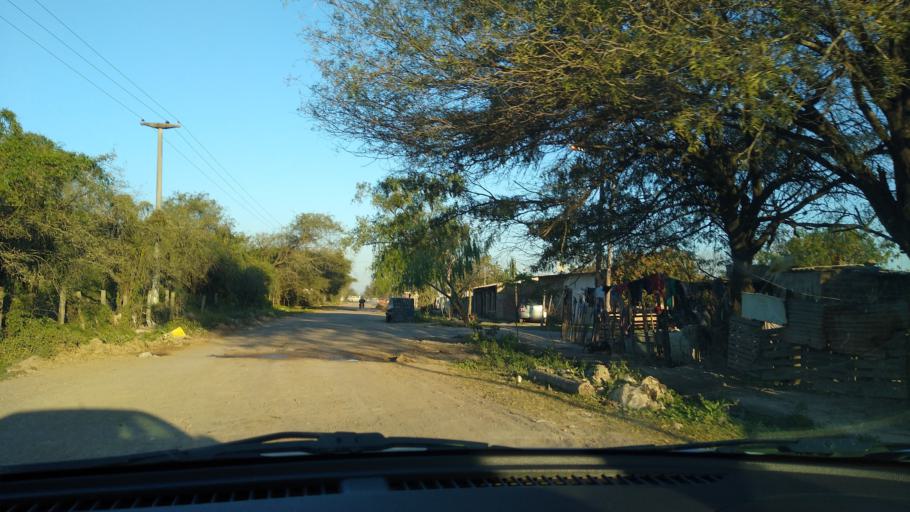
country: AR
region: Chaco
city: Puerto Vilelas
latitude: -27.4970
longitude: -58.9706
